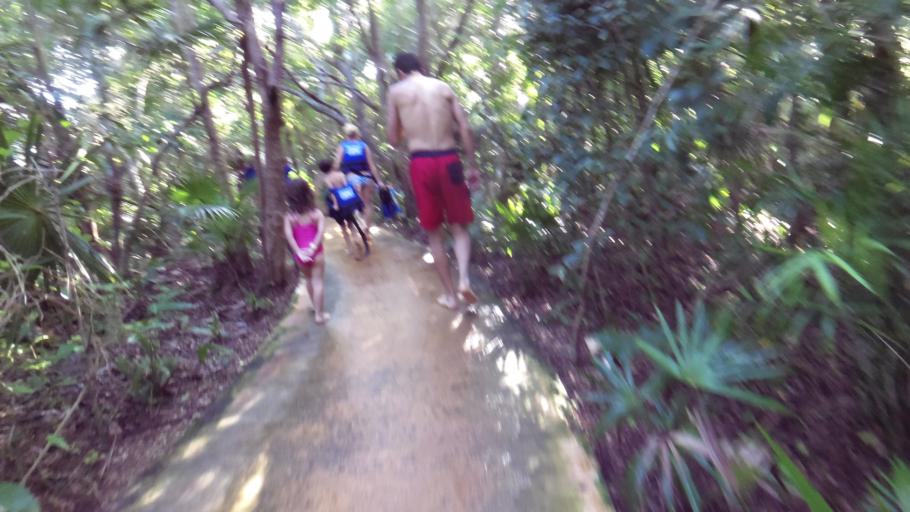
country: MX
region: Quintana Roo
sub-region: Tulum
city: Ciudad Chemuyil
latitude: 20.3176
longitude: -87.3602
